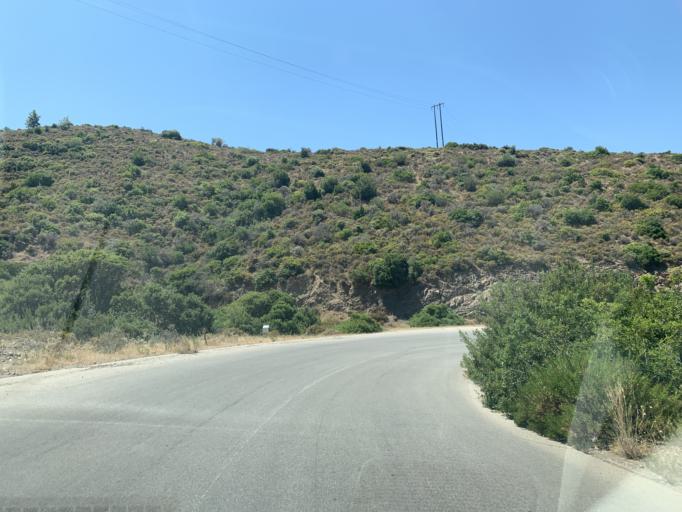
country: GR
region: North Aegean
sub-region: Chios
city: Vrontados
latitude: 38.4691
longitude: 25.9607
